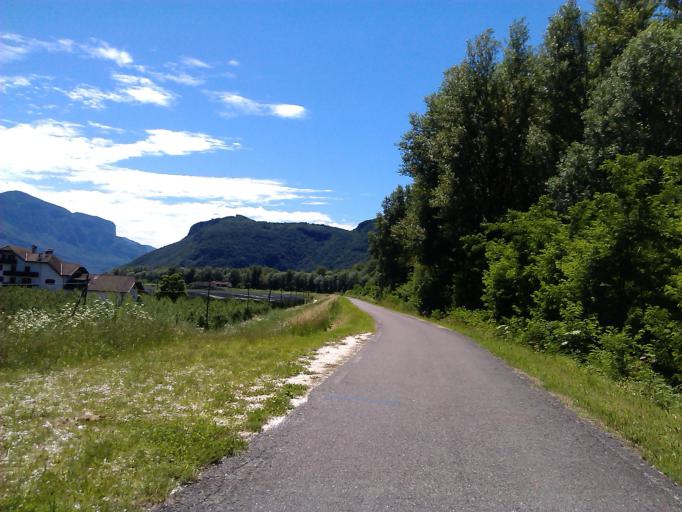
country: IT
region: Trentino-Alto Adige
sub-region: Bolzano
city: Vadena
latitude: 46.3984
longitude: 11.3017
